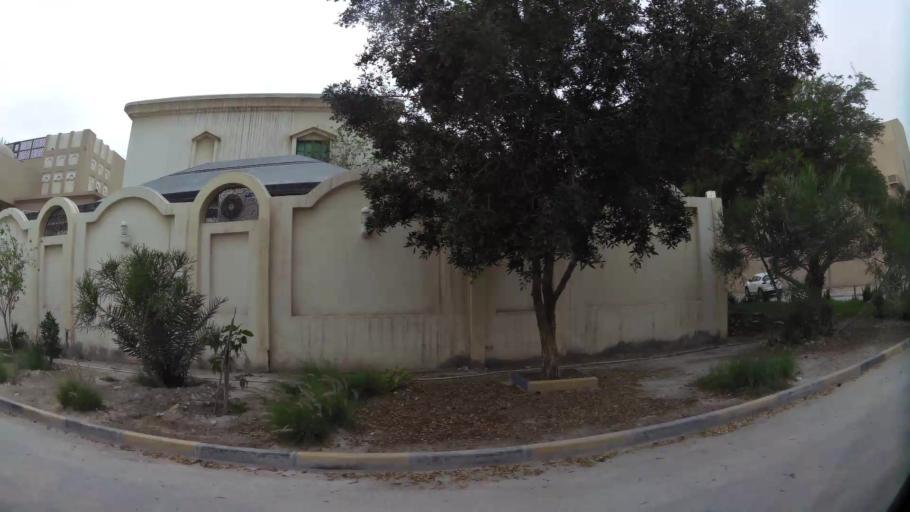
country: QA
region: Baladiyat ad Dawhah
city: Doha
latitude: 25.3084
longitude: 51.5033
